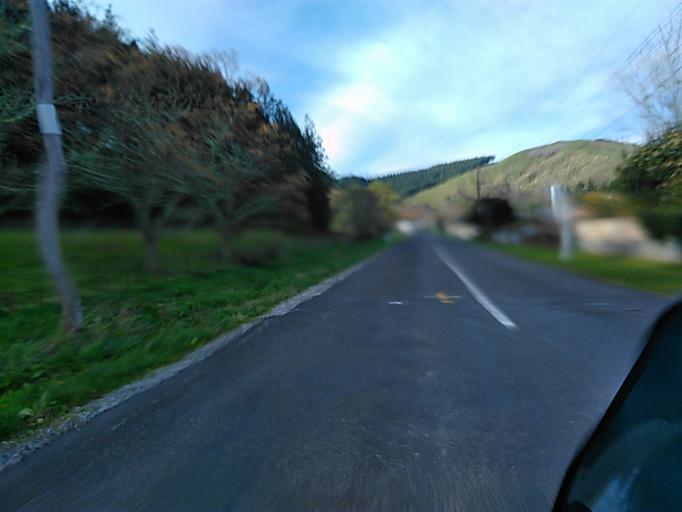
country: NZ
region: Gisborne
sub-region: Gisborne District
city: Gisborne
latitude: -38.6616
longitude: 178.0489
